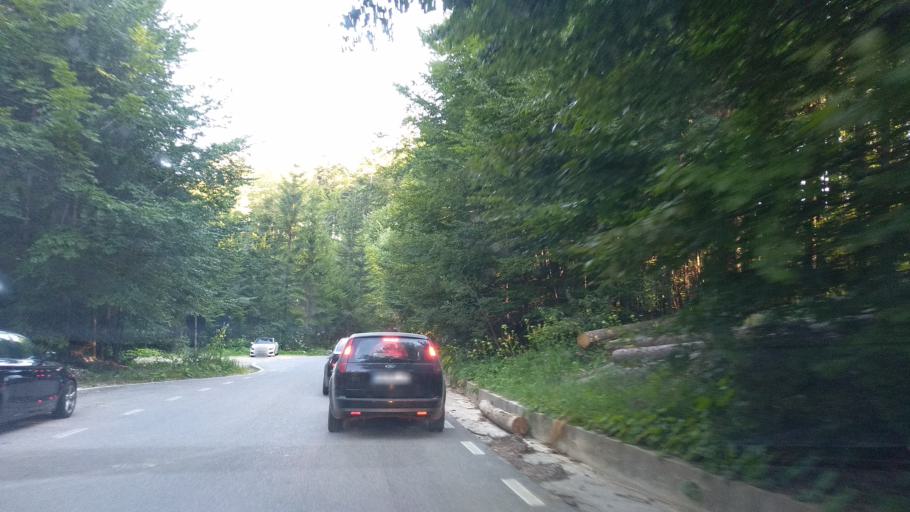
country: RO
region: Prahova
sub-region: Oras Sinaia
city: Sinaia
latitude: 45.3114
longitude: 25.5206
